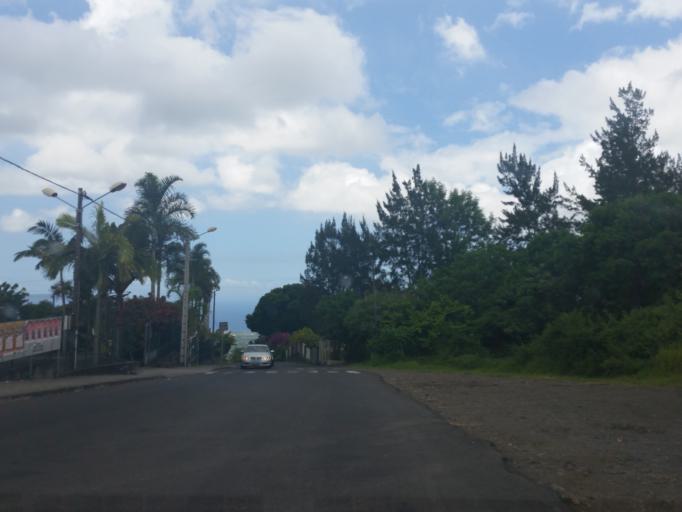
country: RE
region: Reunion
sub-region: Reunion
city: Le Tampon
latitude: -21.2536
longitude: 55.4984
